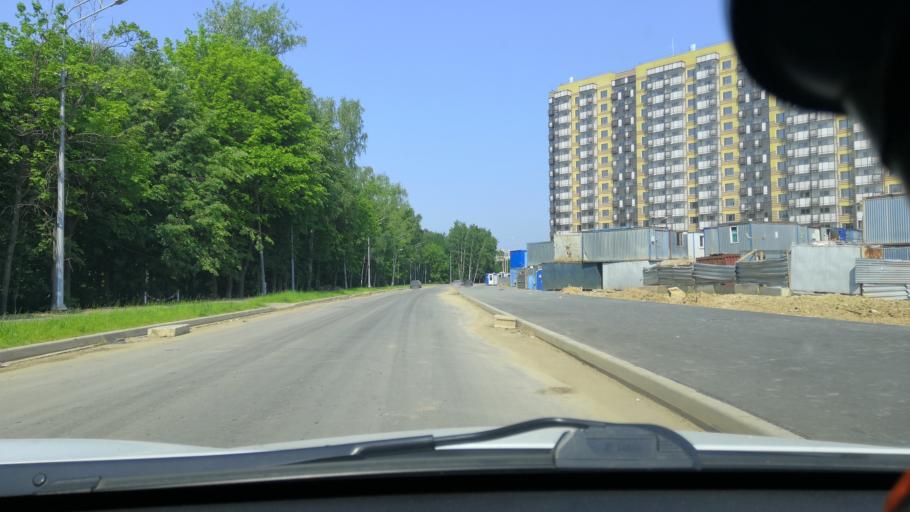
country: RU
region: Moscow
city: Severnyy
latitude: 55.9386
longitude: 37.5272
